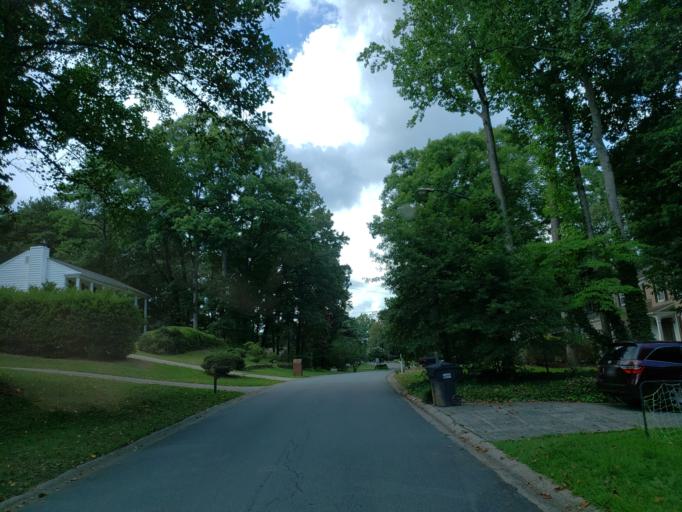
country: US
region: Georgia
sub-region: Fulton County
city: Roswell
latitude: 33.9851
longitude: -84.4209
